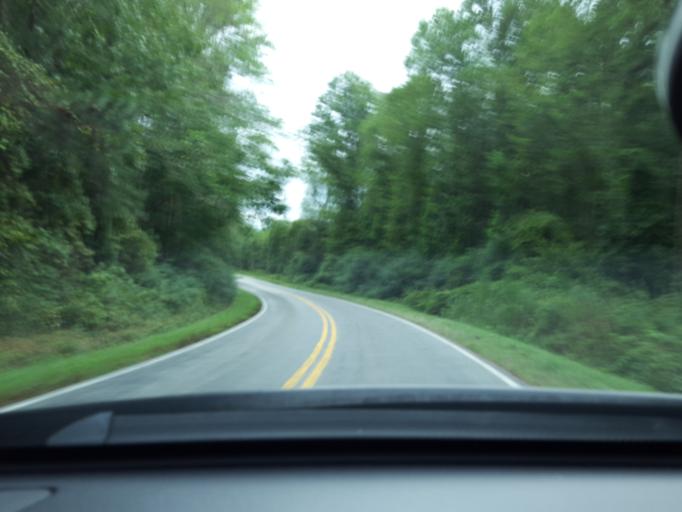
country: US
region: North Carolina
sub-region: Sampson County
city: Roseboro
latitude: 34.7865
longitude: -78.3728
